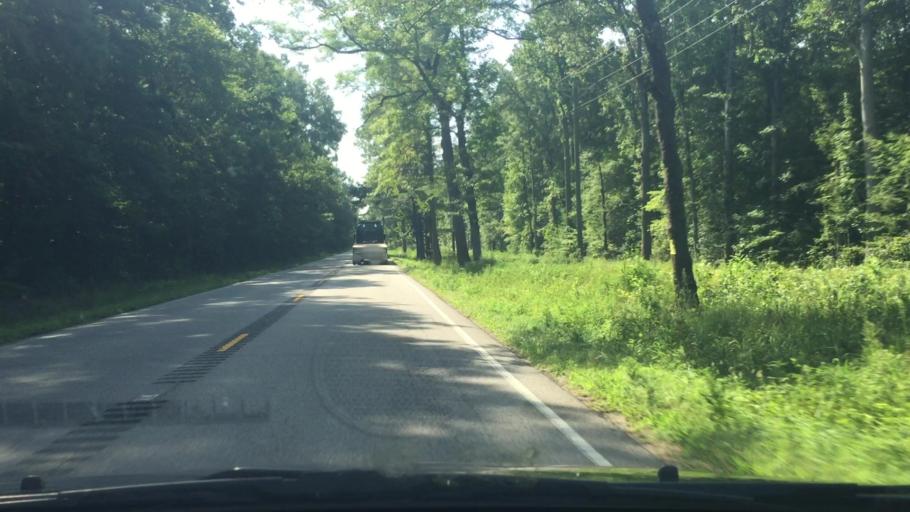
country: US
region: Virginia
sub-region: Sussex County
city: Sussex
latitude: 37.0027
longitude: -77.2667
